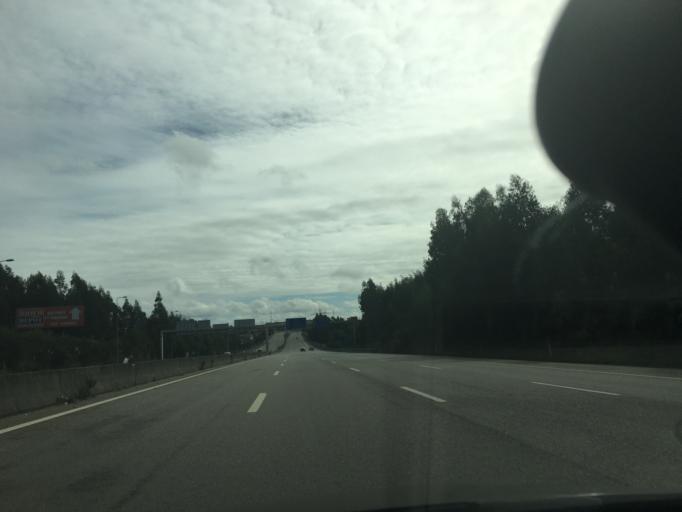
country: PT
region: Porto
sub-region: Matosinhos
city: Guifoes
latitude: 41.2212
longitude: -8.6604
